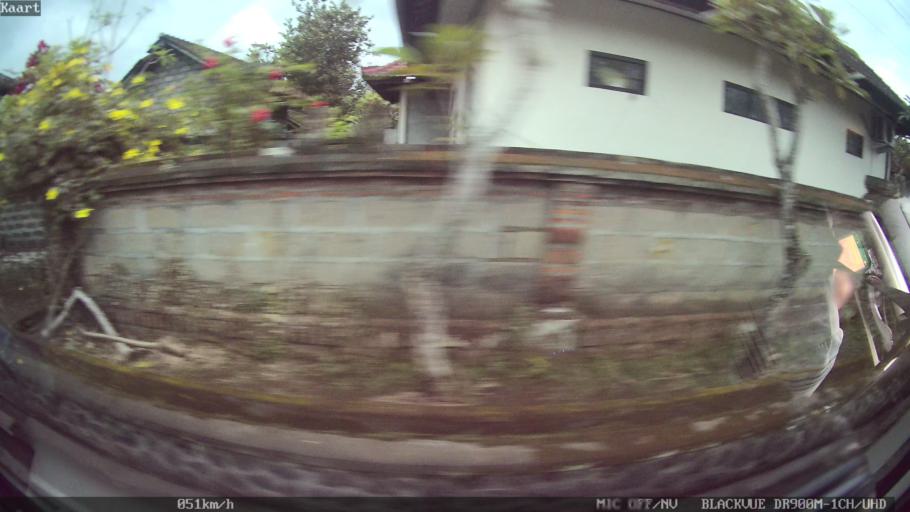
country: ID
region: Bali
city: Banjar Serangan
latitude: -8.5437
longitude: 115.1835
